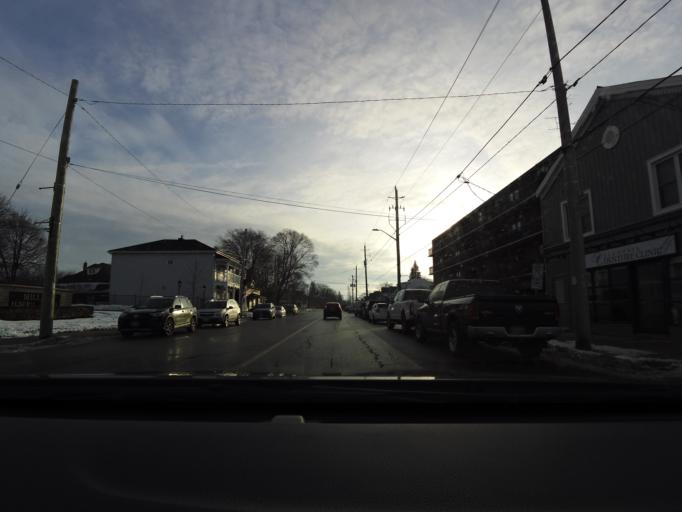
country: CA
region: Ontario
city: Ancaster
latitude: 43.0736
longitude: -79.9508
